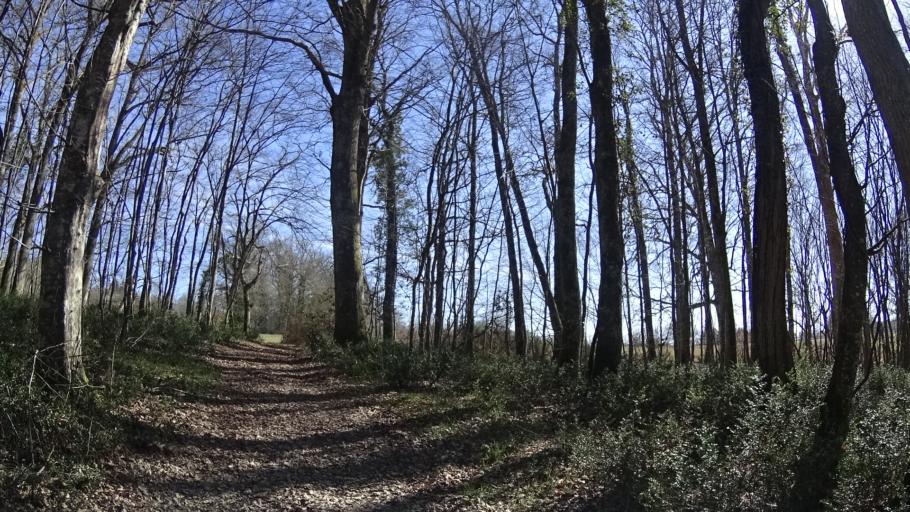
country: FR
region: Aquitaine
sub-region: Departement de la Dordogne
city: Riberac
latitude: 45.1813
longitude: 0.2974
